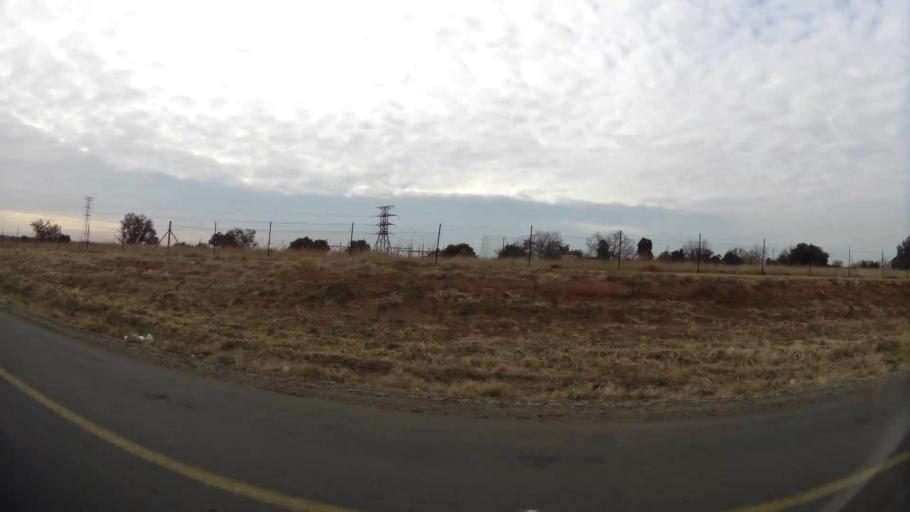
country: ZA
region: Orange Free State
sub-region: Mangaung Metropolitan Municipality
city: Bloemfontein
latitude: -29.1283
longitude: 26.1645
